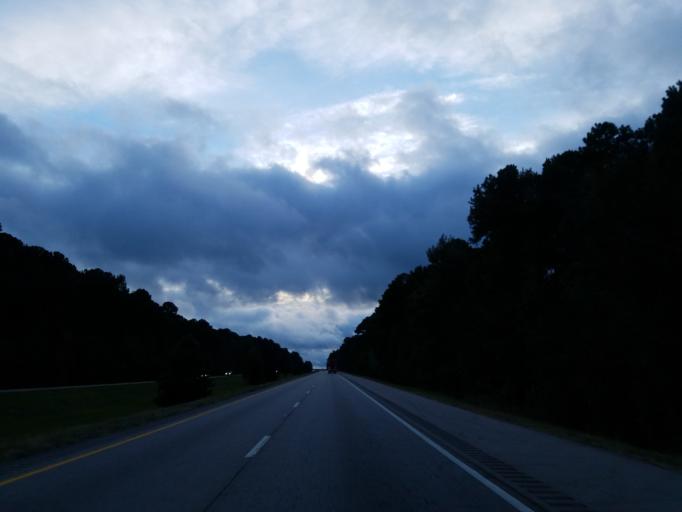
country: US
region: Mississippi
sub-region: Lauderdale County
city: Marion
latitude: 32.4072
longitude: -88.5431
